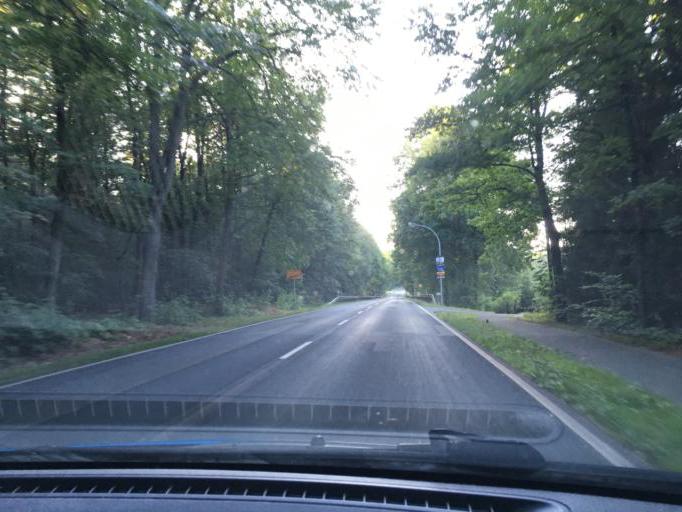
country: DE
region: Lower Saxony
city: Unterluss
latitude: 52.7950
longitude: 10.3836
